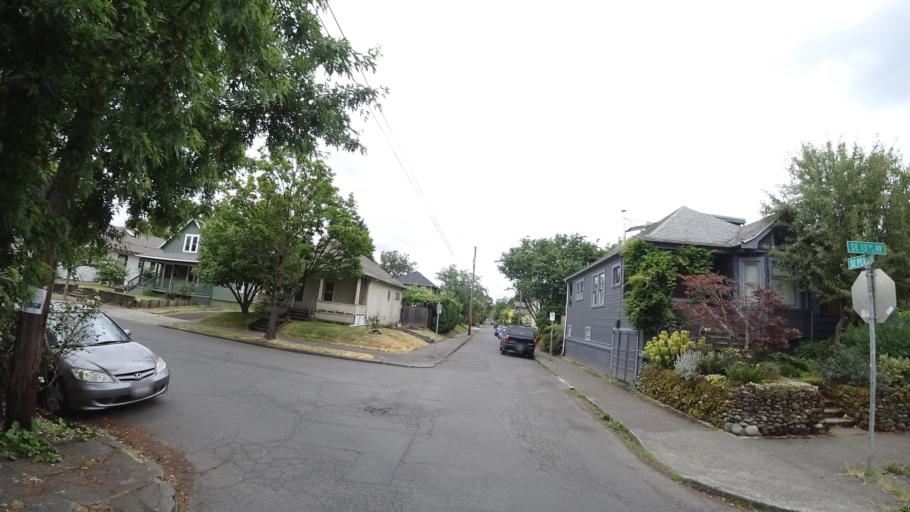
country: US
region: Oregon
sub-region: Multnomah County
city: Portland
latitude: 45.4989
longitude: -122.6523
